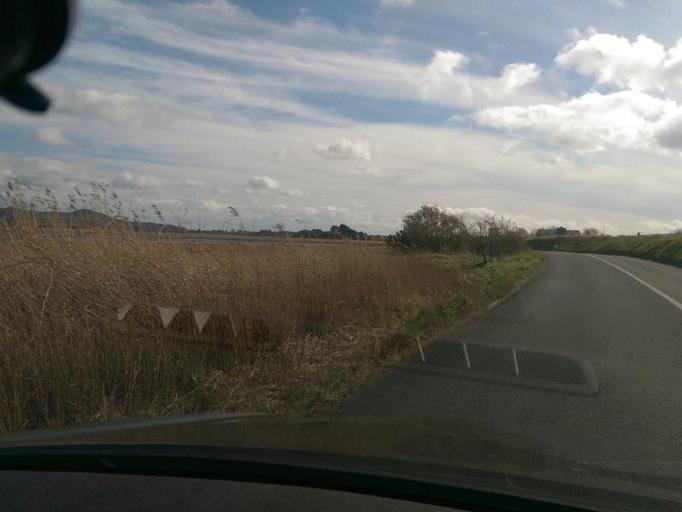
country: IE
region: Leinster
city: Portmarnock
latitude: 53.4118
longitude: -6.1371
